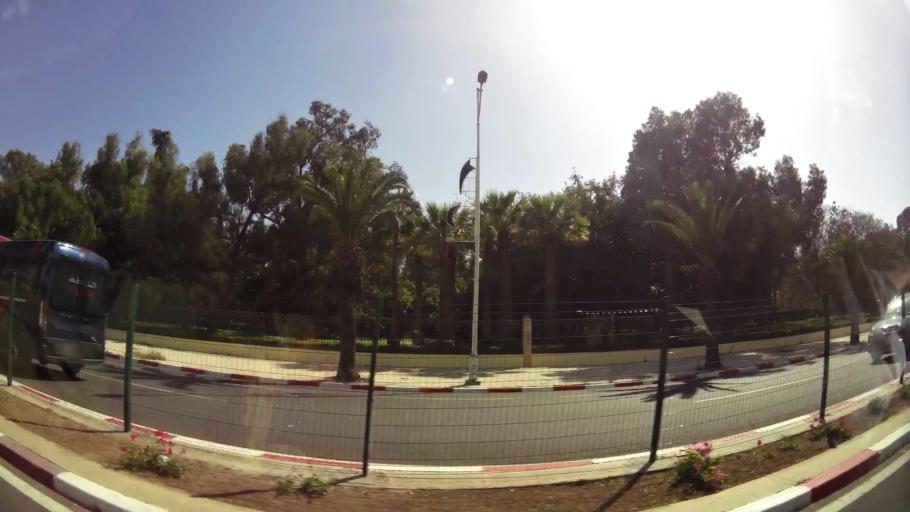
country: MA
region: Souss-Massa-Draa
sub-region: Agadir-Ida-ou-Tnan
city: Agadir
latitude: 30.4104
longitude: -9.5922
